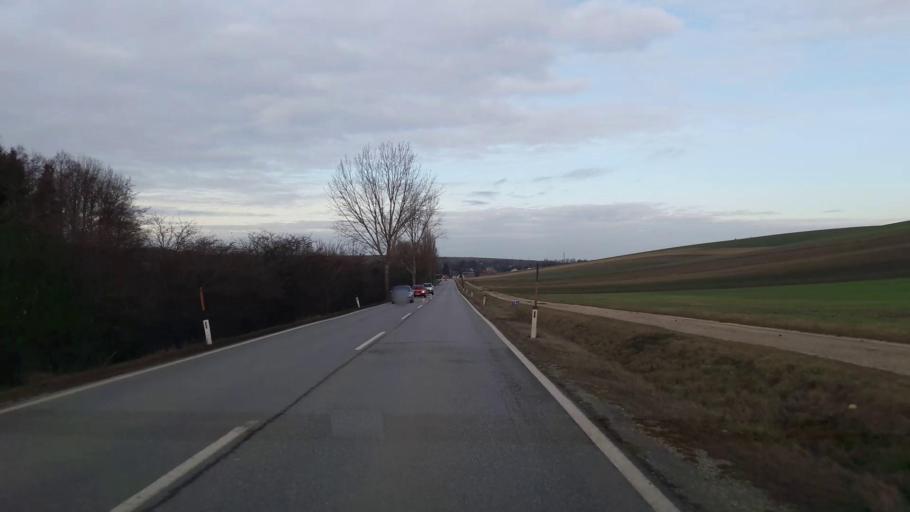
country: AT
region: Lower Austria
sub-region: Politischer Bezirk Mistelbach
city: Staatz
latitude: 48.6531
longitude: 16.5031
